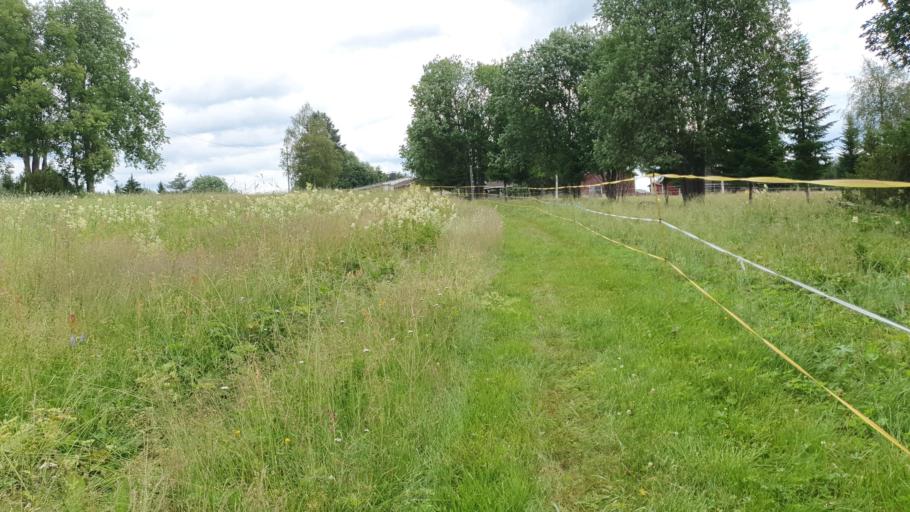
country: FI
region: Kainuu
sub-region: Kehys-Kainuu
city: Kuhmo
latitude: 64.7322
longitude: 29.6381
